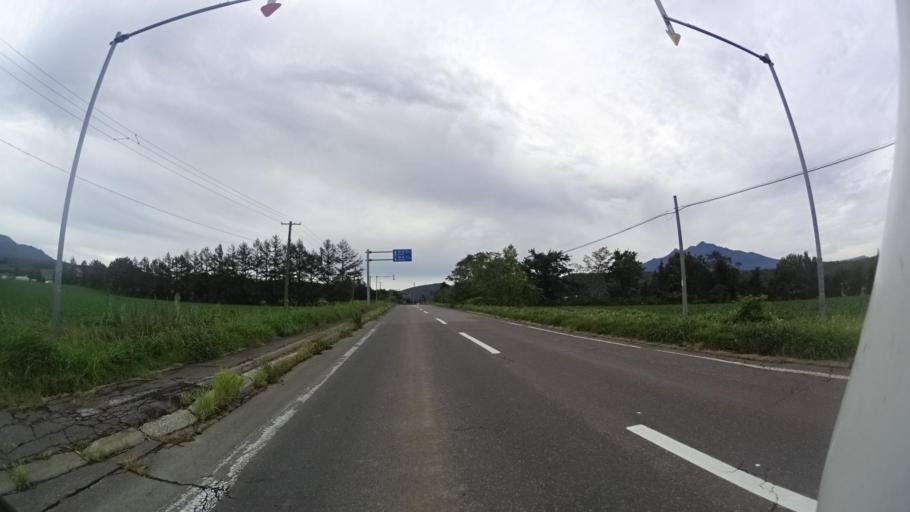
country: JP
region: Hokkaido
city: Shibetsu
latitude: 43.8736
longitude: 144.7472
